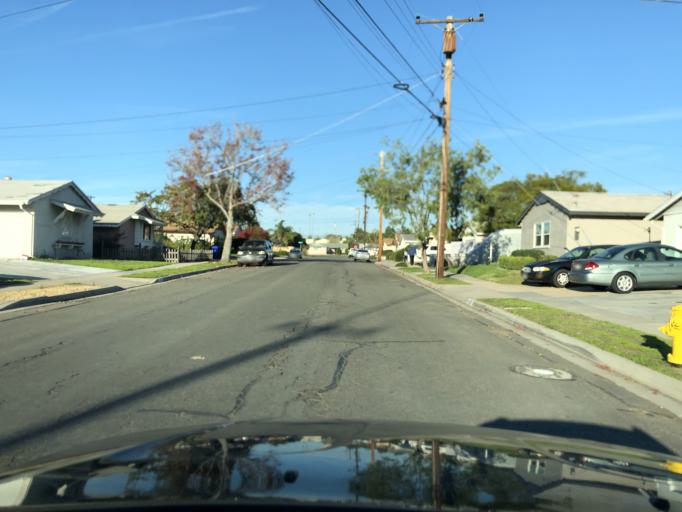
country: US
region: California
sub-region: San Diego County
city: La Jolla
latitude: 32.8198
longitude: -117.1888
